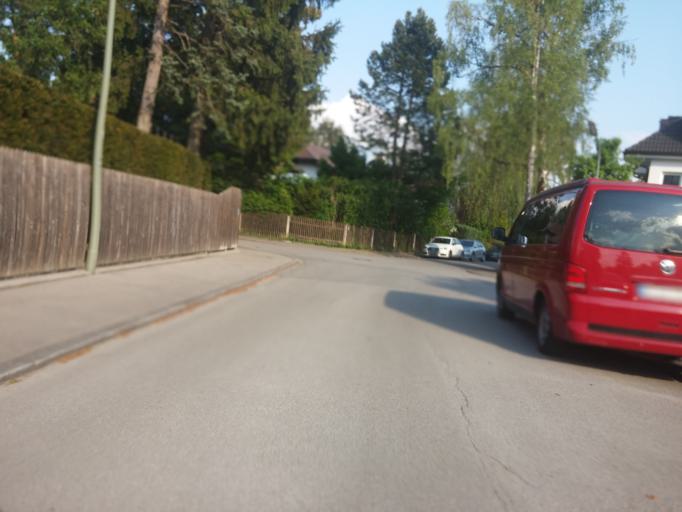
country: DE
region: Bavaria
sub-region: Upper Bavaria
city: Haar
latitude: 48.1078
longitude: 11.7028
